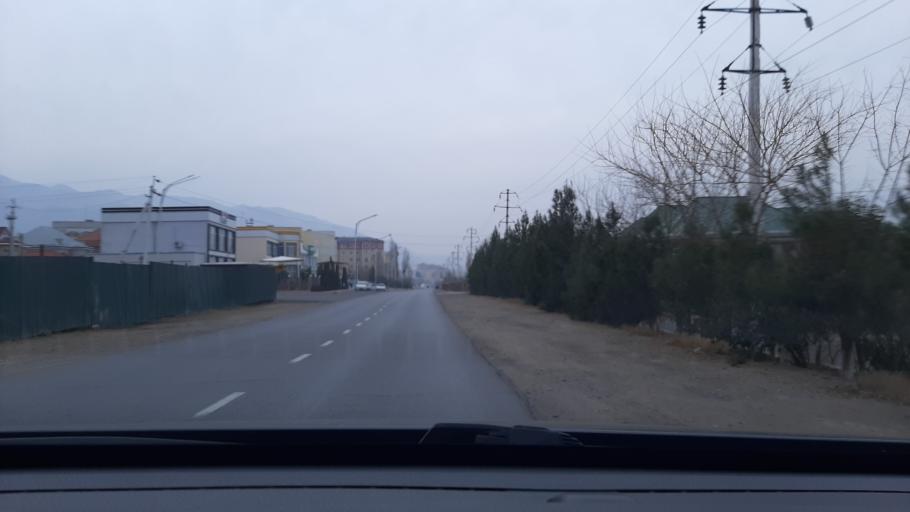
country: TJ
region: Viloyati Sughd
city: Khujand
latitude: 40.2788
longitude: 69.5829
